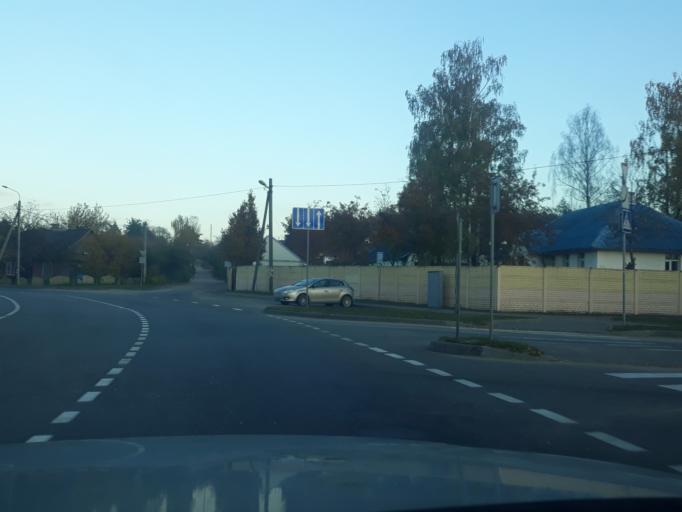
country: BY
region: Grodnenskaya
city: Vawkavysk
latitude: 53.1484
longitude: 24.4364
